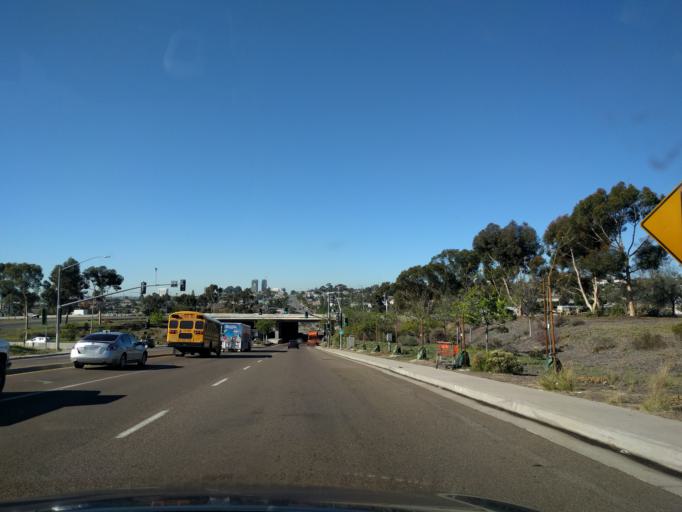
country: US
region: California
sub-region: San Diego County
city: National City
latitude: 32.7116
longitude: -117.1170
